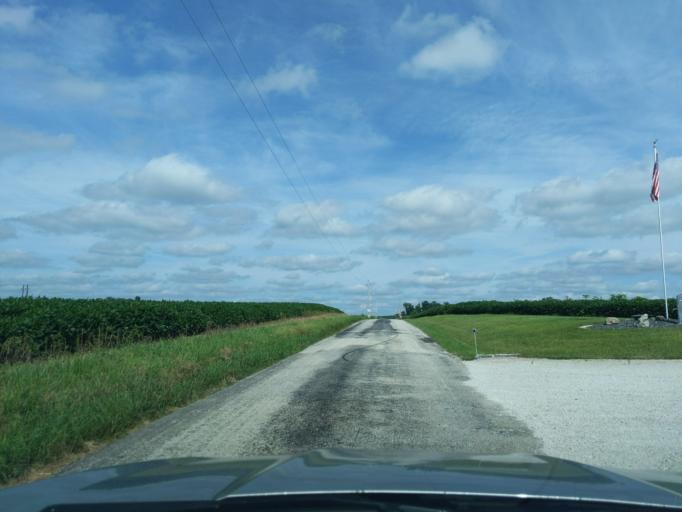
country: US
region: Indiana
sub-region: Ripley County
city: Osgood
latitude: 39.2351
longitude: -85.3776
